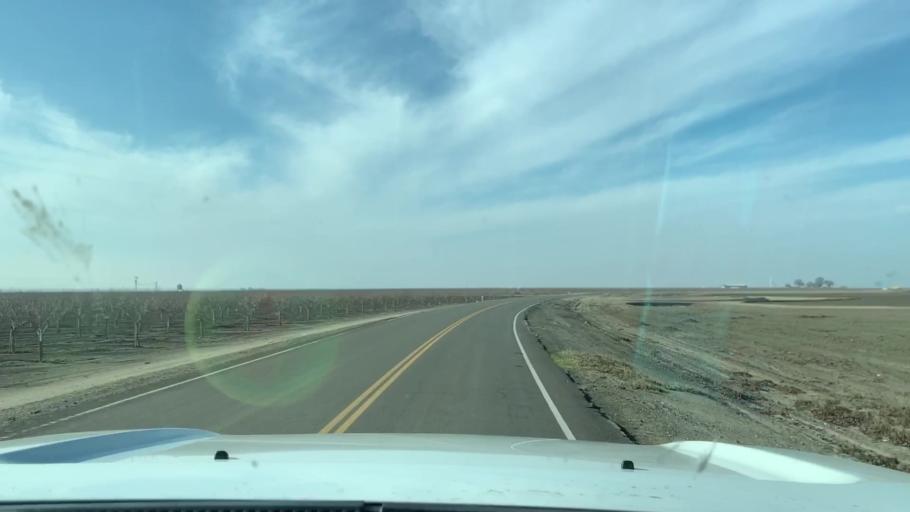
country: US
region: California
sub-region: Kern County
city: Buttonwillow
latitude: 35.4475
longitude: -119.5586
